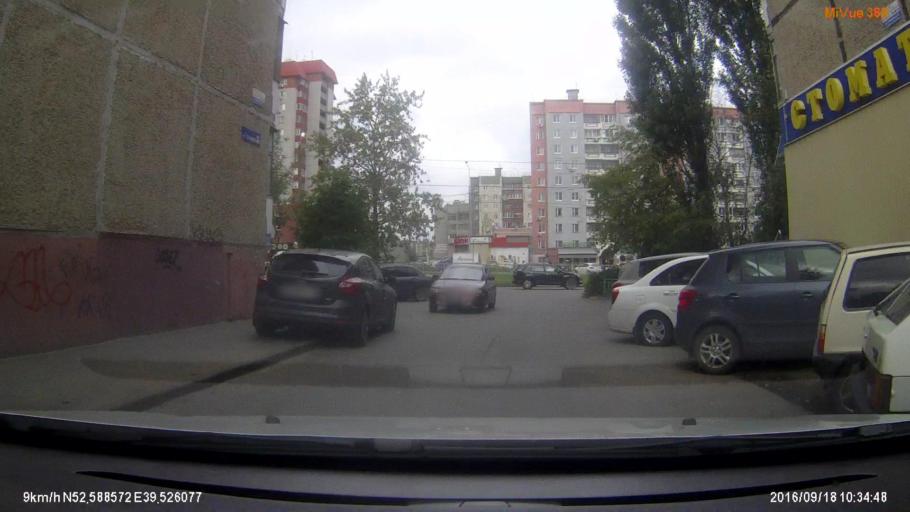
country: RU
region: Lipetsk
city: Syrskoye
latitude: 52.5884
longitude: 39.5305
